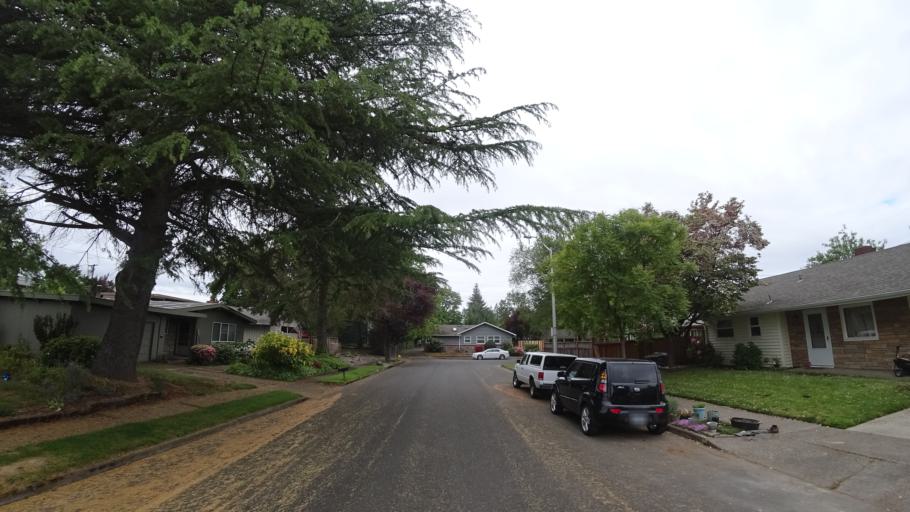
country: US
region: Oregon
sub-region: Washington County
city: Beaverton
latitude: 45.4774
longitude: -122.8037
